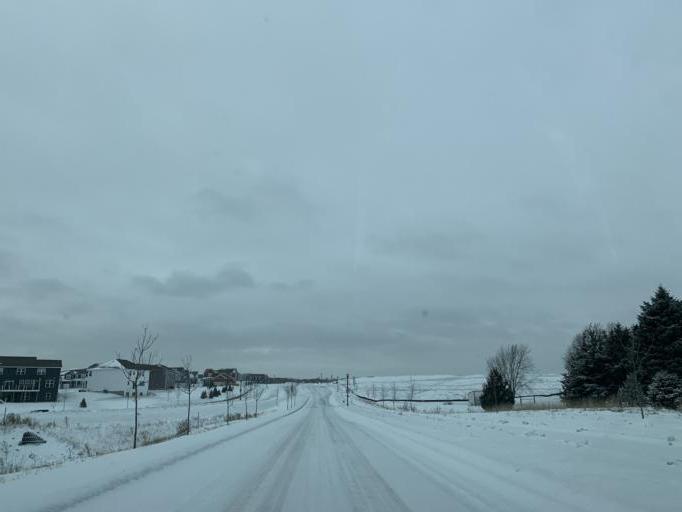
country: US
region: Minnesota
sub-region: Washington County
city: Cottage Grove
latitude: 44.8551
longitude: -92.9149
